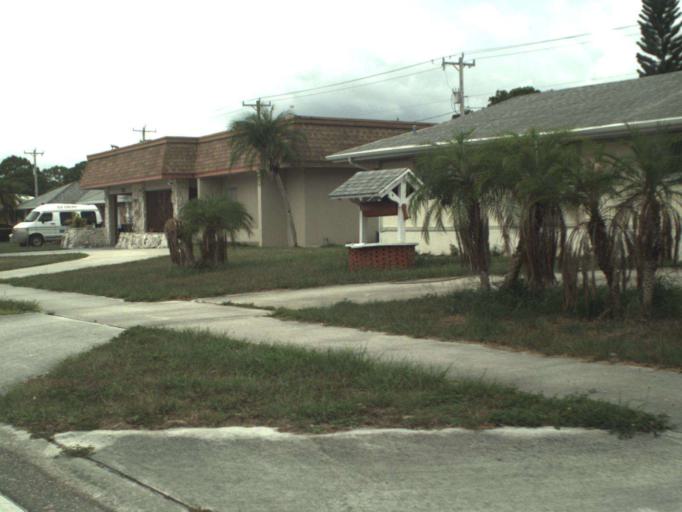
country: US
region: Florida
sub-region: Saint Lucie County
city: River Park
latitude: 27.3206
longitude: -80.3497
